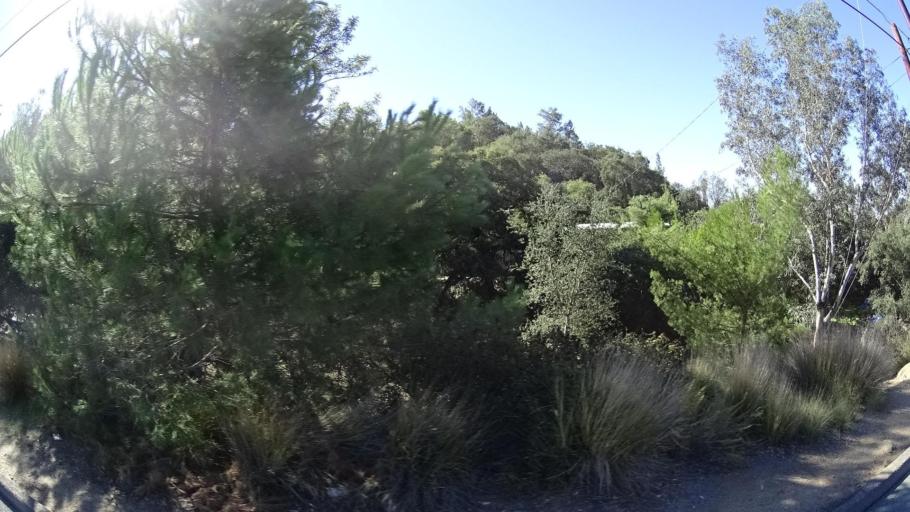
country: US
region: California
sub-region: San Diego County
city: Jamul
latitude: 32.7316
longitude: -116.8369
